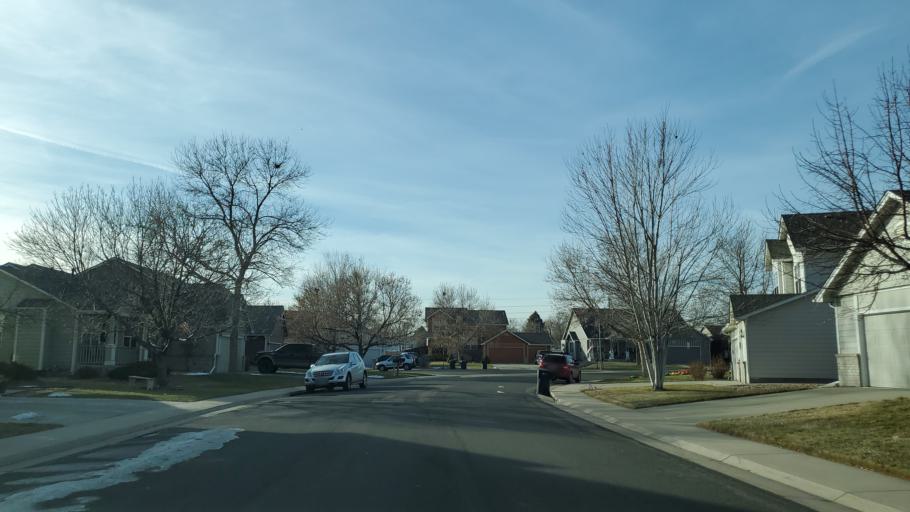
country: US
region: Colorado
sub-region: Adams County
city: Northglenn
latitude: 39.9053
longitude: -104.9574
